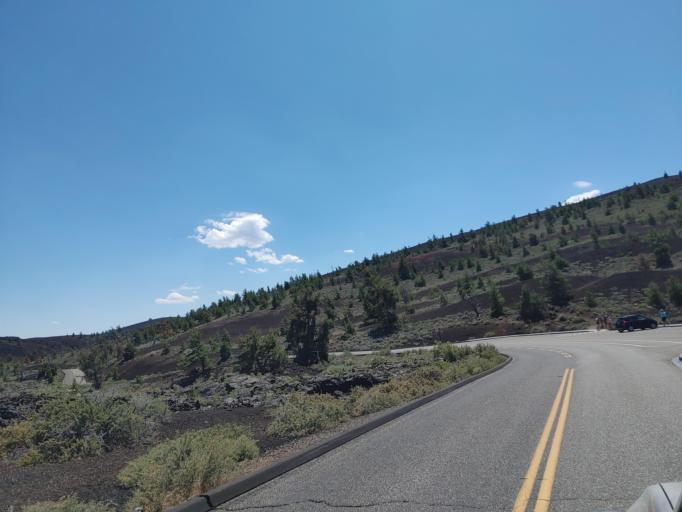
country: US
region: Idaho
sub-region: Butte County
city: Arco
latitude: 43.4567
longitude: -113.5590
